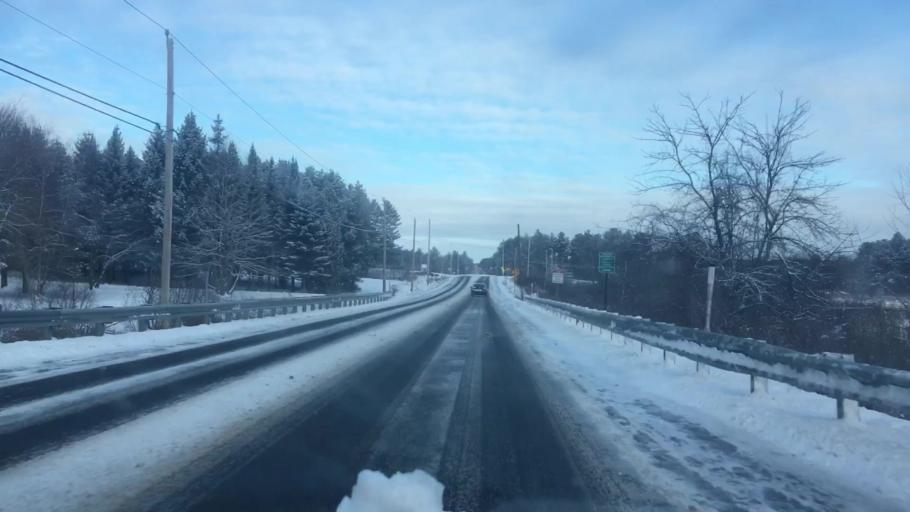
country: US
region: Maine
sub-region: Cumberland County
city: North Windham
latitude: 43.7962
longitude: -70.4401
